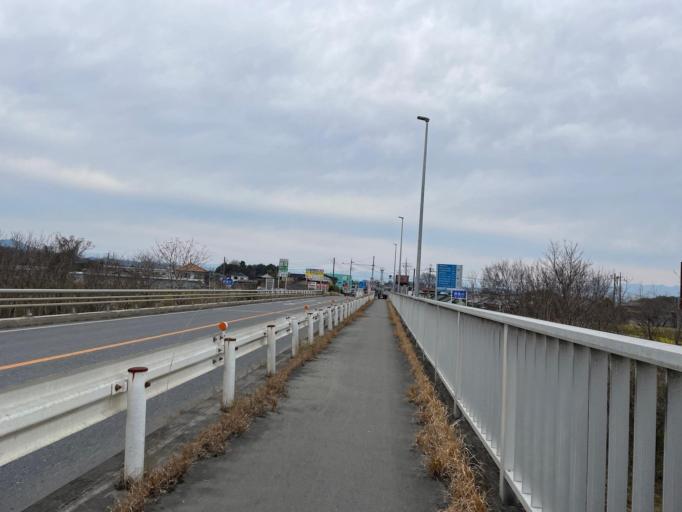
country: JP
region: Gunma
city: Fujioka
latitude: 36.2382
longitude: 139.0936
